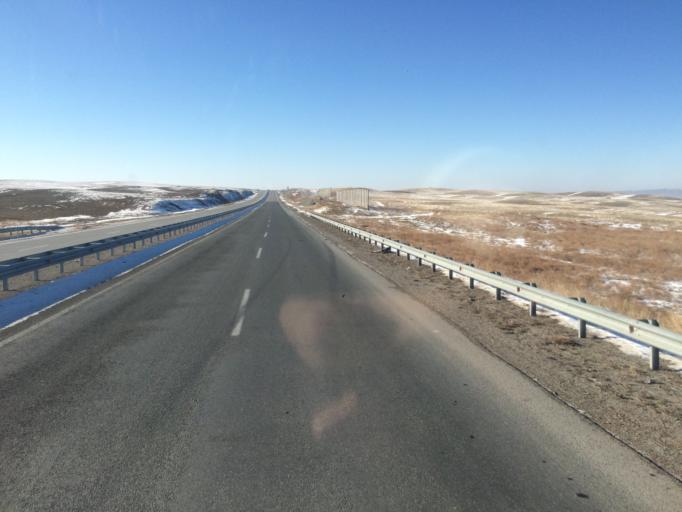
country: KZ
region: Zhambyl
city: Georgiyevka
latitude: 43.3638
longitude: 74.6996
